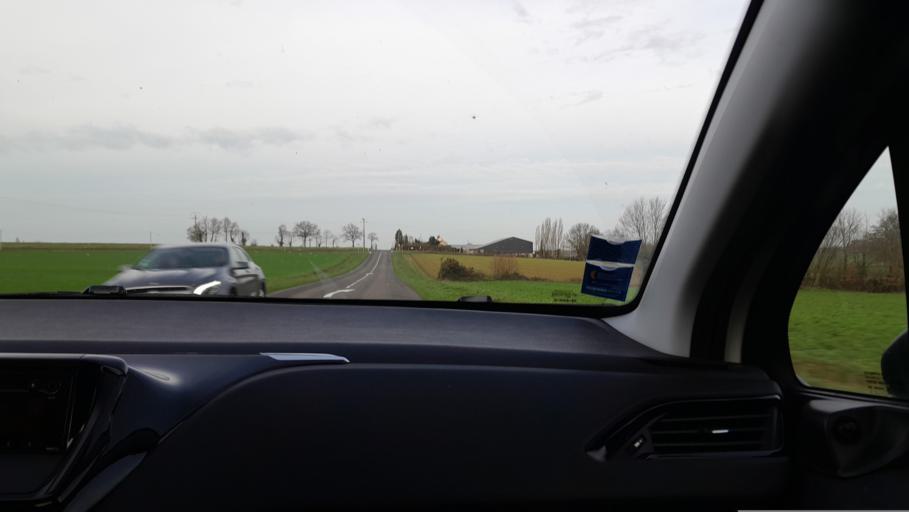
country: FR
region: Pays de la Loire
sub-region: Departement de la Mayenne
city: Craon
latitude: 47.8660
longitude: -0.9898
